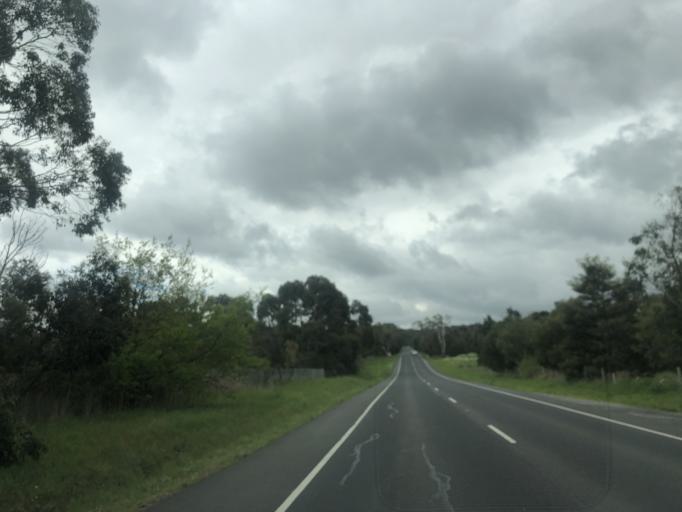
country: AU
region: Victoria
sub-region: Casey
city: Endeavour Hills
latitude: -37.9596
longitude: 145.2493
